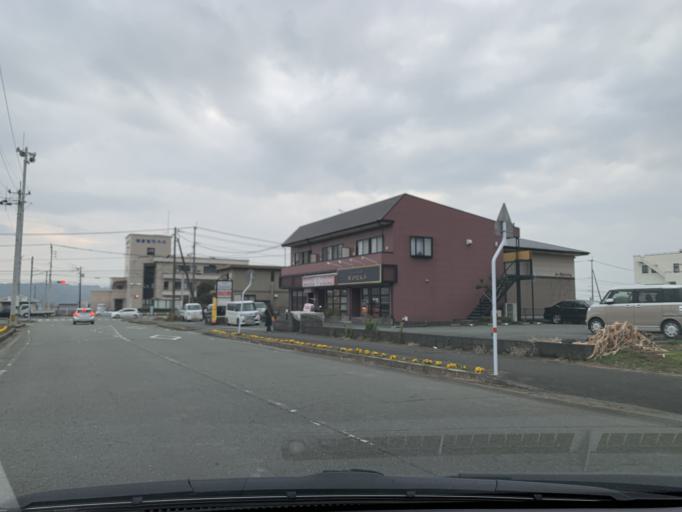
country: JP
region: Kumamoto
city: Ozu
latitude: 32.8764
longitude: 130.8633
